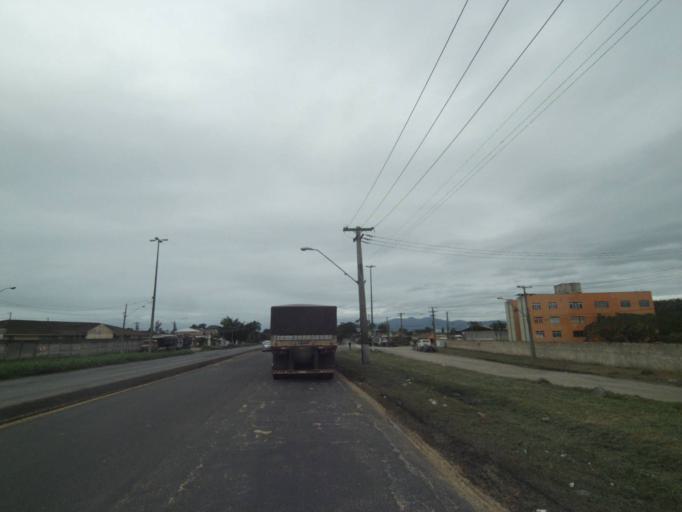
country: BR
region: Parana
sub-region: Paranagua
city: Paranagua
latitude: -25.5320
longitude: -48.5295
